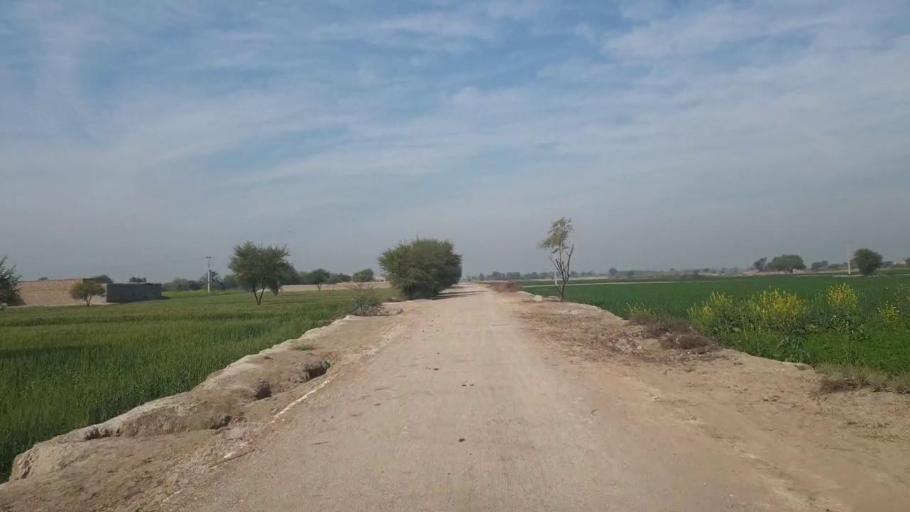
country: PK
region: Sindh
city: Nawabshah
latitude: 26.1632
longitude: 68.5028
